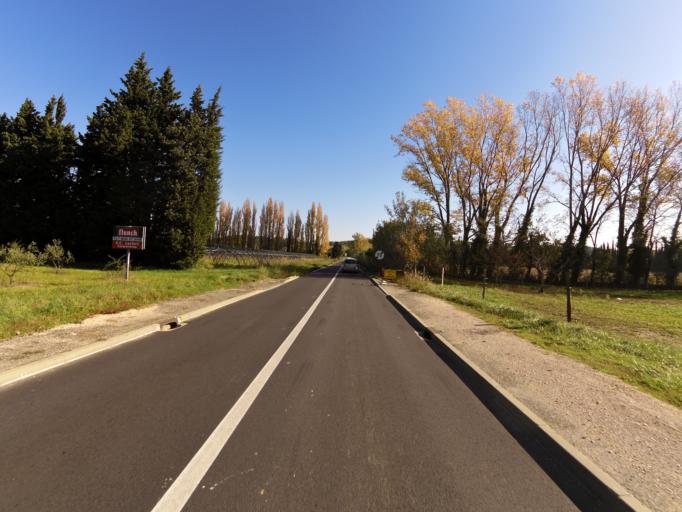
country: FR
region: Provence-Alpes-Cote d'Azur
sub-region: Departement du Vaucluse
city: Loriol-du-Comtat
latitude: 44.0749
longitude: 4.9986
